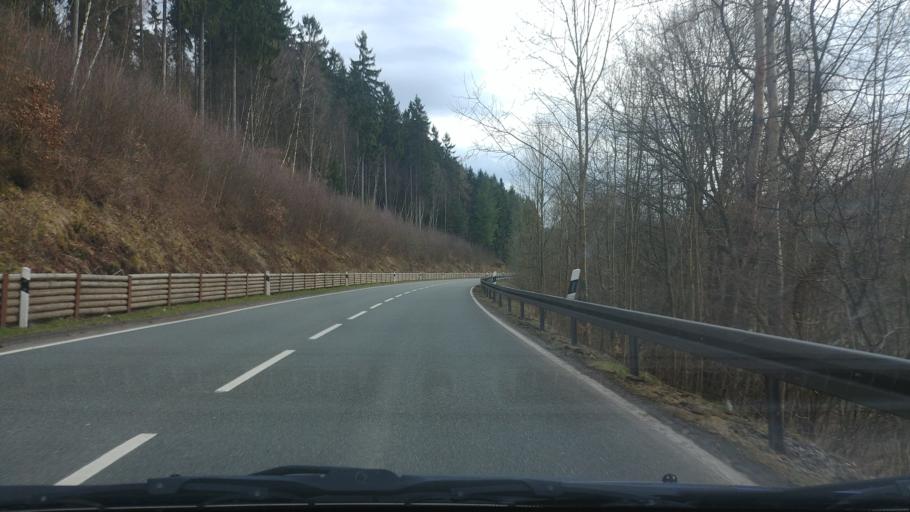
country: DE
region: Lower Saxony
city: Bevern
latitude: 51.8123
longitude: 9.4940
